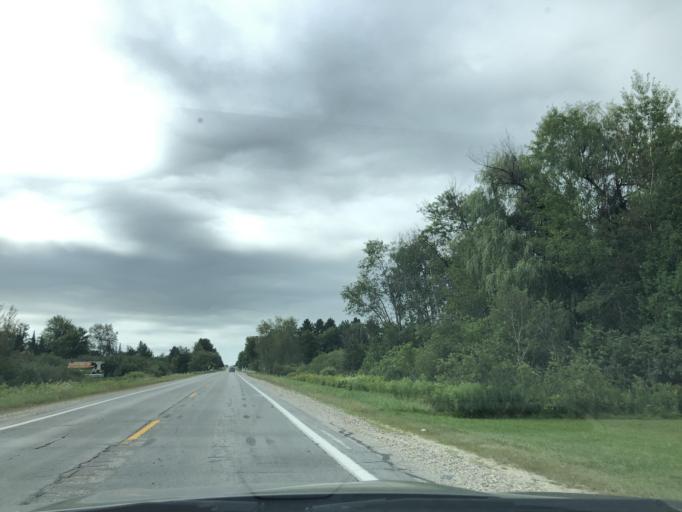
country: US
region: Michigan
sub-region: Missaukee County
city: Lake City
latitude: 44.2452
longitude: -85.2152
